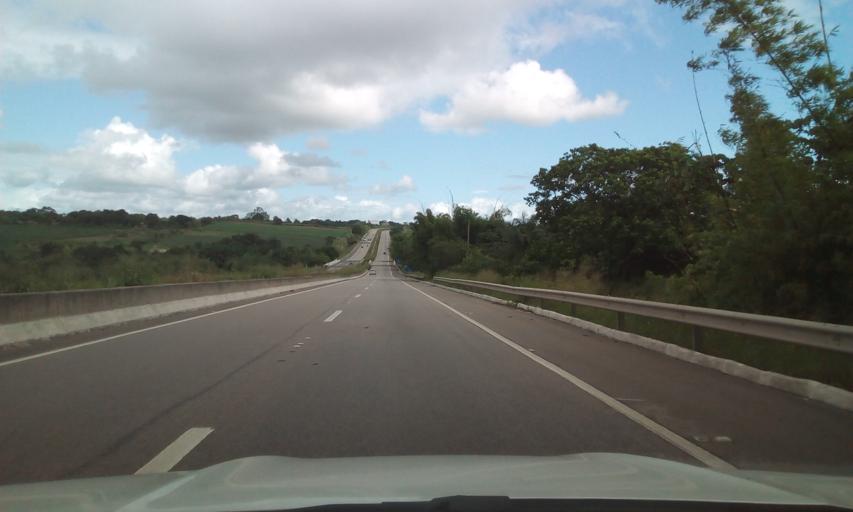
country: BR
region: Pernambuco
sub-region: Itapissuma
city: Itapissuma
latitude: -7.6878
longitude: -34.9225
